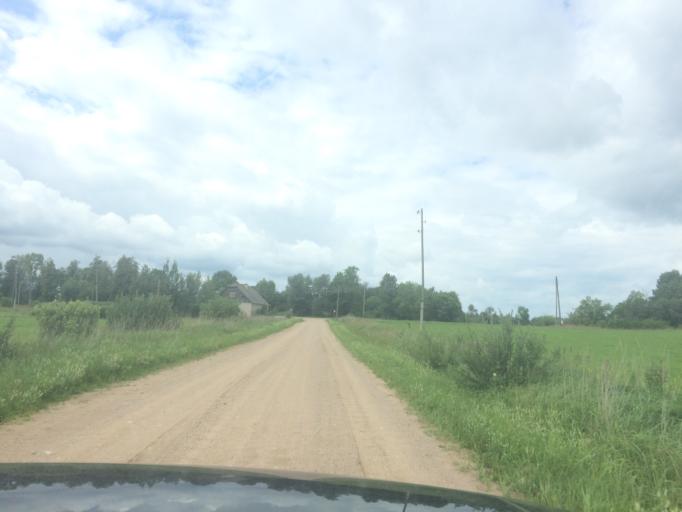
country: LV
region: Rezekne
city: Rezekne
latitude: 56.6615
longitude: 27.2700
